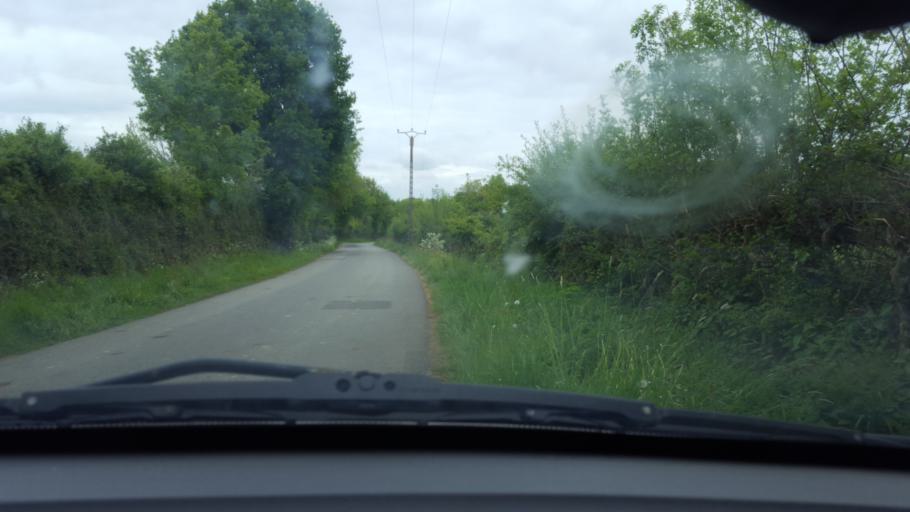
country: FR
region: Pays de la Loire
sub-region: Departement de la Loire-Atlantique
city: La Limouziniere
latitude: 47.0197
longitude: -1.5996
